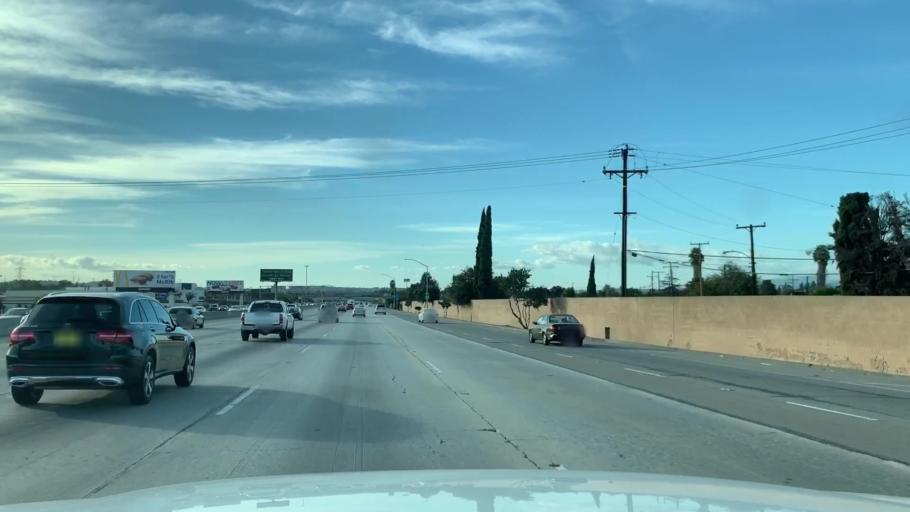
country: US
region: California
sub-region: Los Angeles County
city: South El Monte
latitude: 34.0380
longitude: -118.0409
